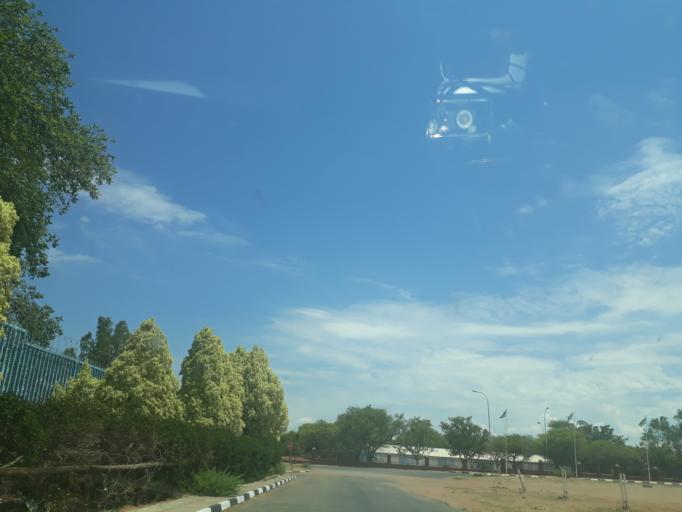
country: BW
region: South East
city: Gaborone
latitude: -24.6574
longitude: 25.9317
